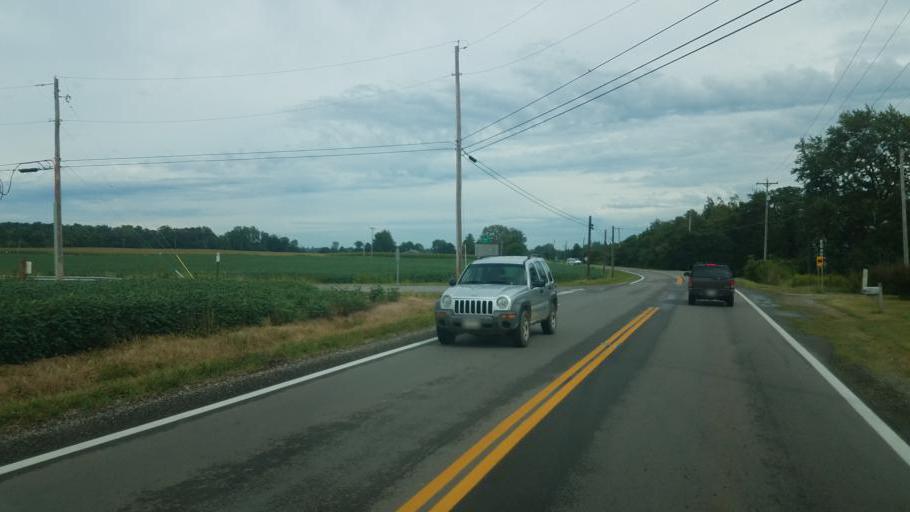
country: US
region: Ohio
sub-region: Morrow County
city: Cardington
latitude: 40.5167
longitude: -82.8648
